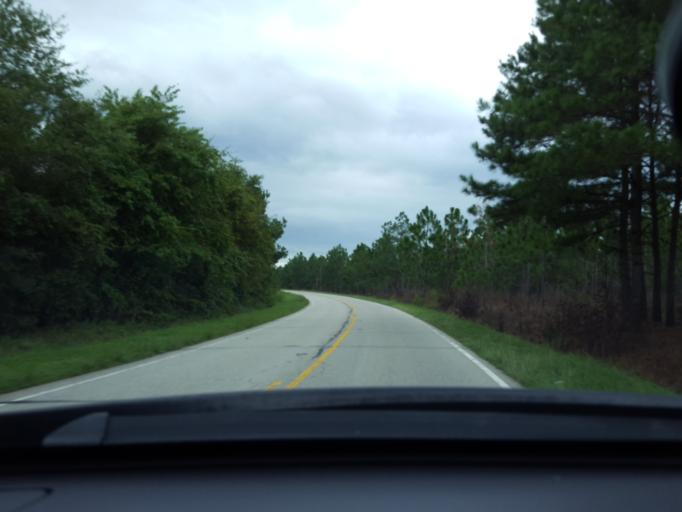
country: US
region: North Carolina
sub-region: Sampson County
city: Clinton
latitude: 34.8007
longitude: -78.2643
